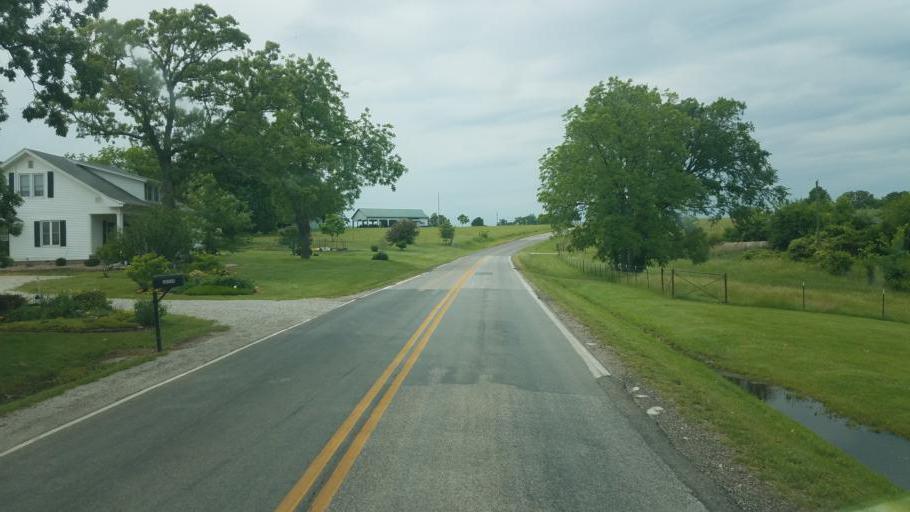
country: US
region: Missouri
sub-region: Moniteau County
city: California
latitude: 38.6573
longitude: -92.5770
